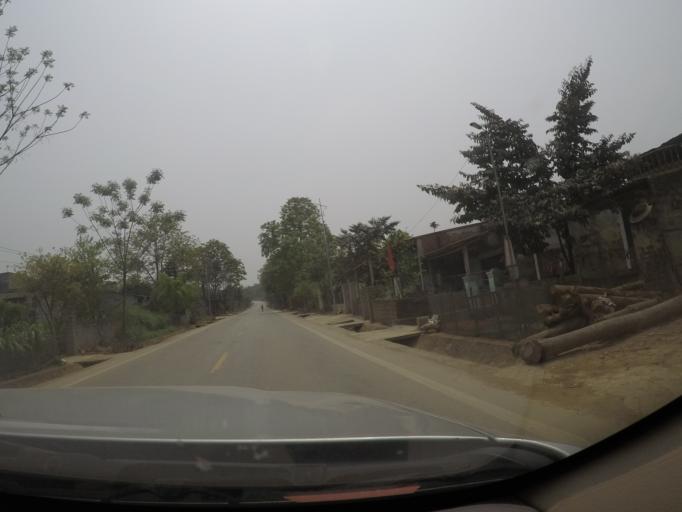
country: VN
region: Thanh Hoa
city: Thi Tran Thuong Xuan
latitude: 19.8829
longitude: 105.4067
